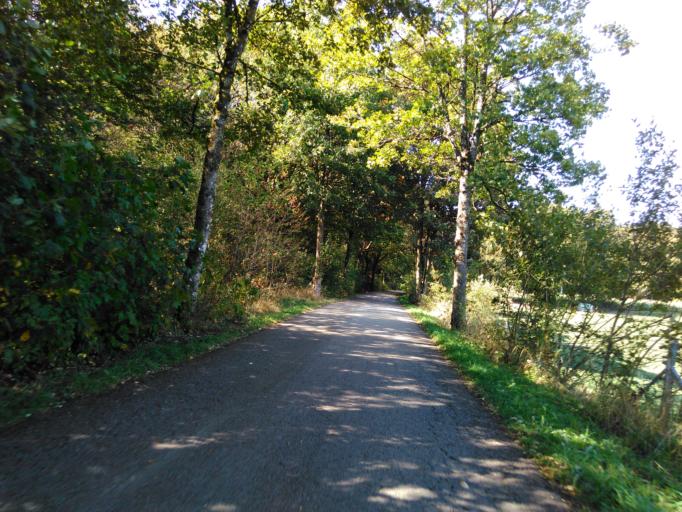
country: LU
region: Diekirch
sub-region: Canton de Redange
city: Rambrouch
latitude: 49.8150
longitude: 5.8365
